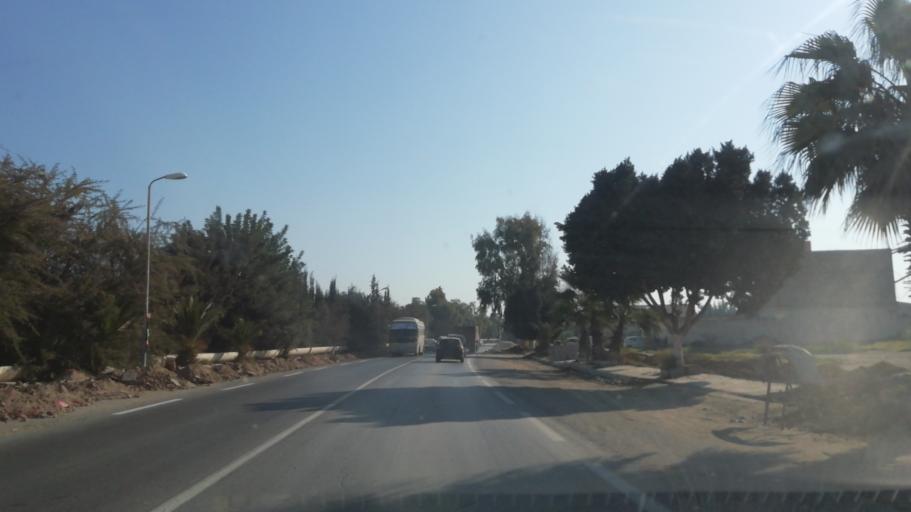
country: DZ
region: Relizane
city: Relizane
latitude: 35.7342
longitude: 0.4669
